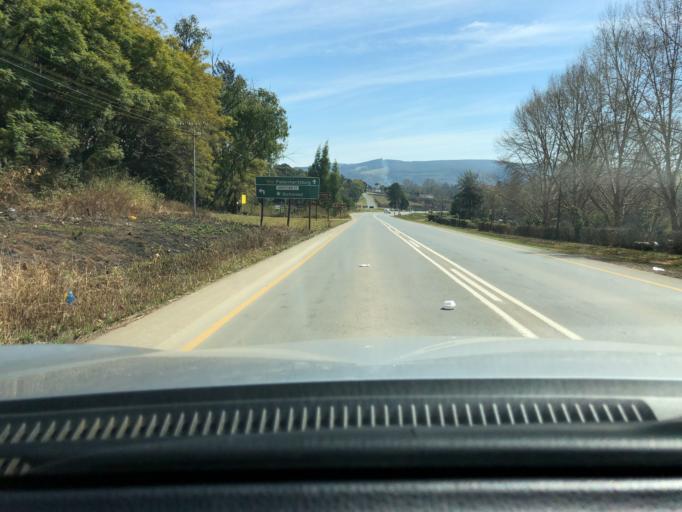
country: ZA
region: KwaZulu-Natal
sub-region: uMgungundlovu District Municipality
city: Richmond
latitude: -29.8804
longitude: 30.2850
